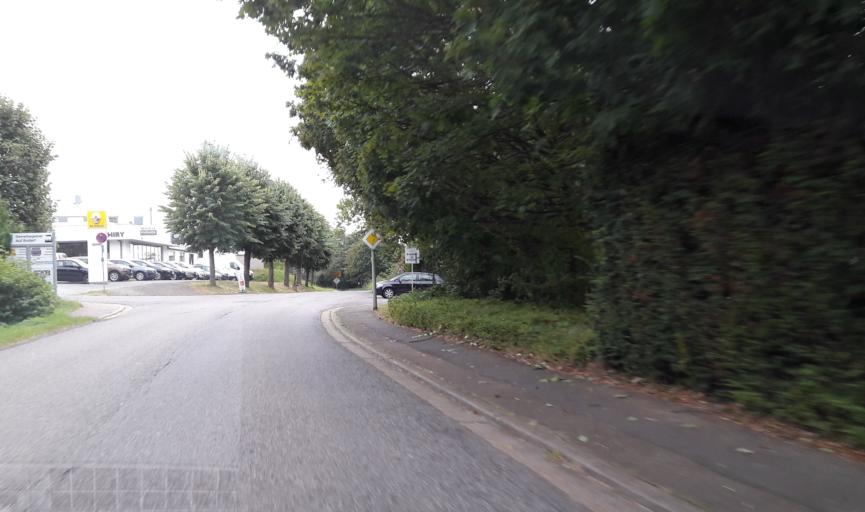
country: DE
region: Saarland
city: Tholey
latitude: 49.4768
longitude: 7.0377
